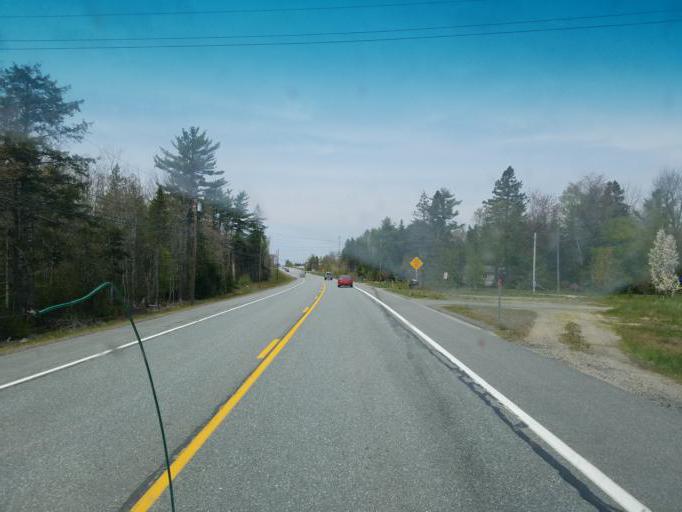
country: US
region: Maine
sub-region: Hancock County
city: Surry
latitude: 44.6117
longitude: -68.5215
